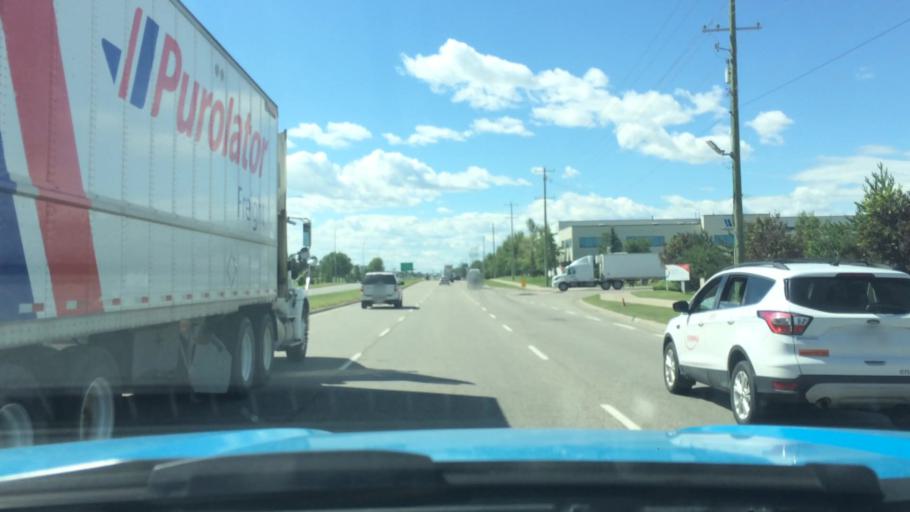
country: CA
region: Alberta
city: Calgary
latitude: 50.9977
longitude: -113.9587
